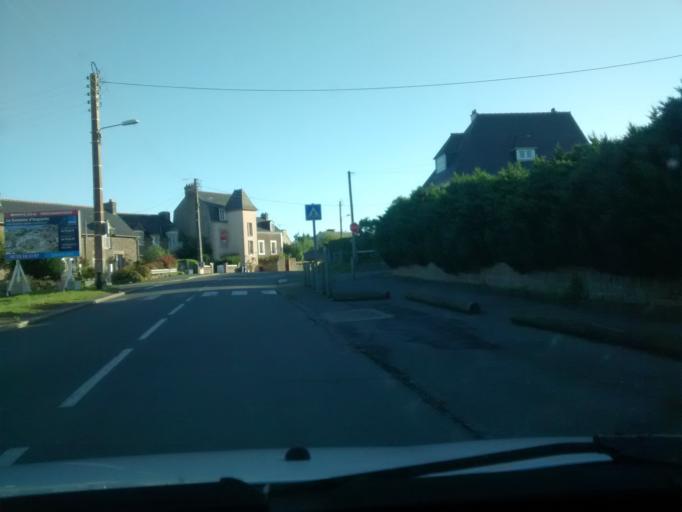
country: FR
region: Brittany
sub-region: Departement d'Ille-et-Vilaine
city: Saint-Malo
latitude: 48.6796
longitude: -1.9777
